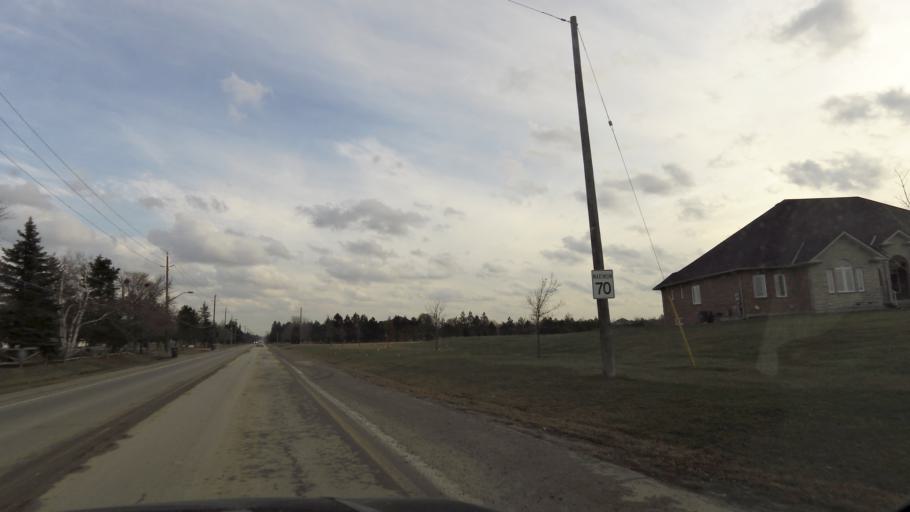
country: CA
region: Ontario
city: Brampton
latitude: 43.8011
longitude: -79.7257
